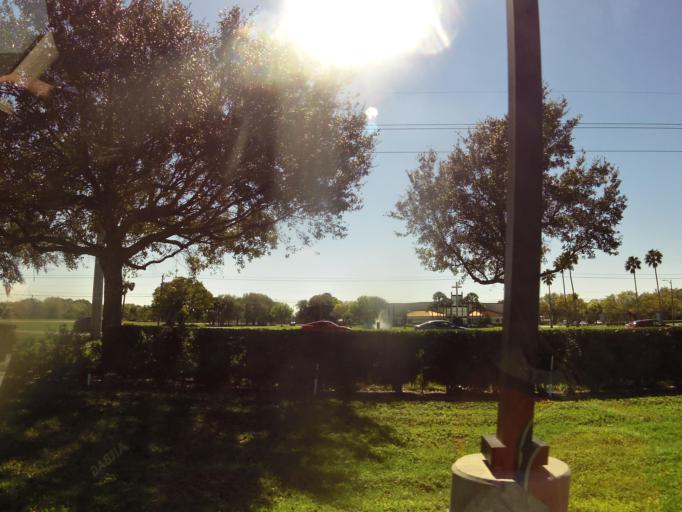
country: US
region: Florida
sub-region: Seminole County
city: Sanford
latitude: 28.8119
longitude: -81.3038
